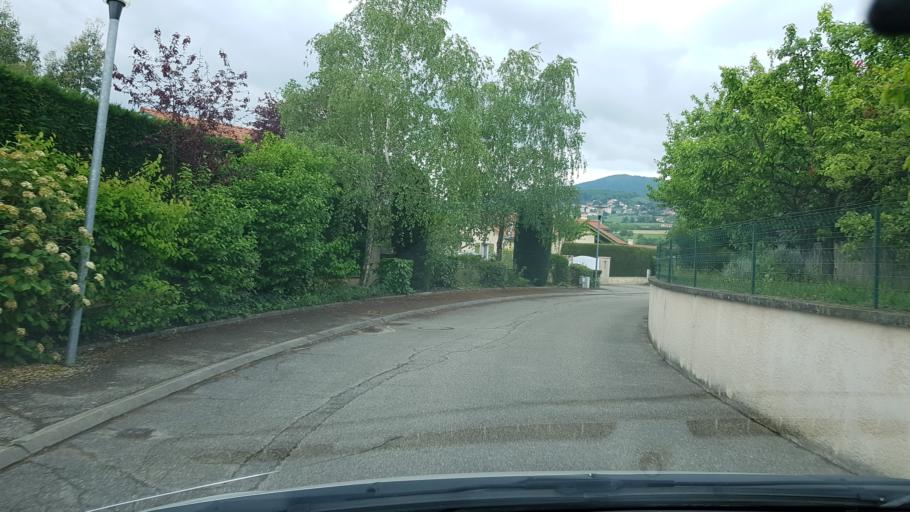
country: FR
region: Rhone-Alpes
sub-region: Departement du Rhone
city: Mornant
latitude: 45.6245
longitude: 4.6658
